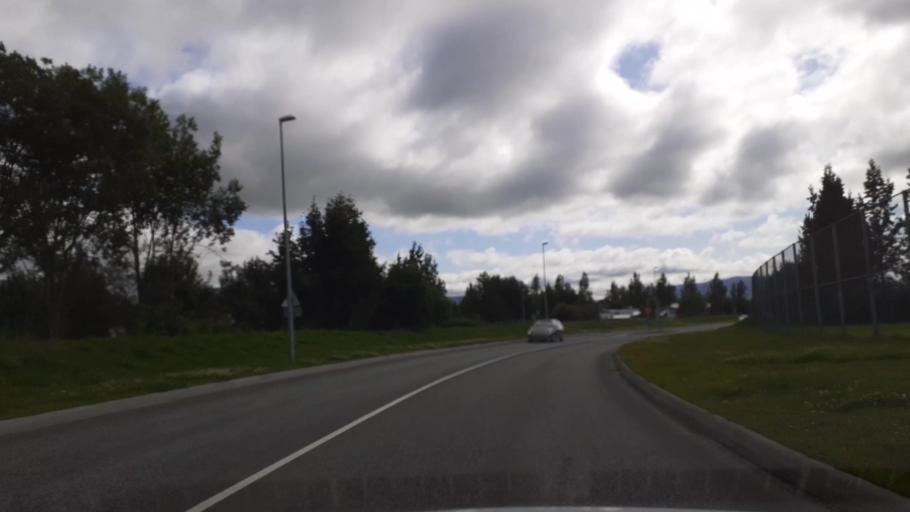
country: IS
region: Northeast
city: Akureyri
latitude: 65.6763
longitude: -18.1110
